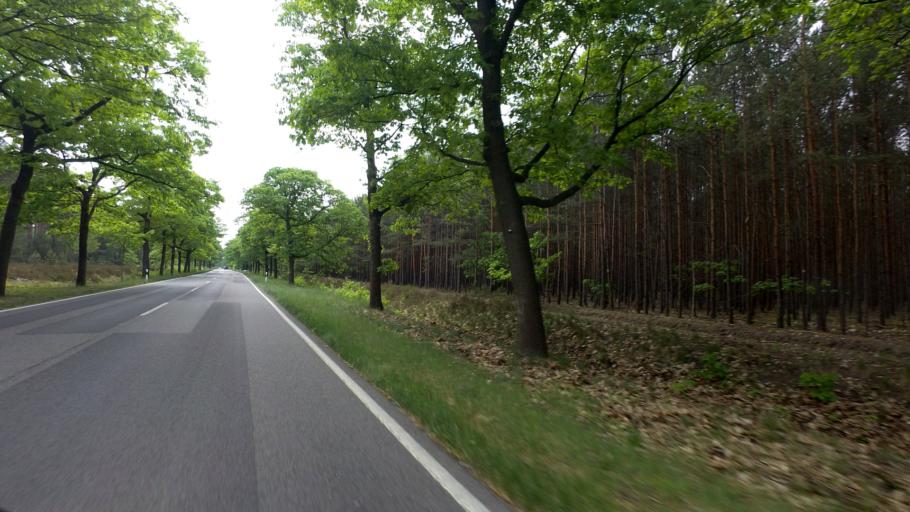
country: DE
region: Brandenburg
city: Drachhausen
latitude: 51.9229
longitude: 14.3476
